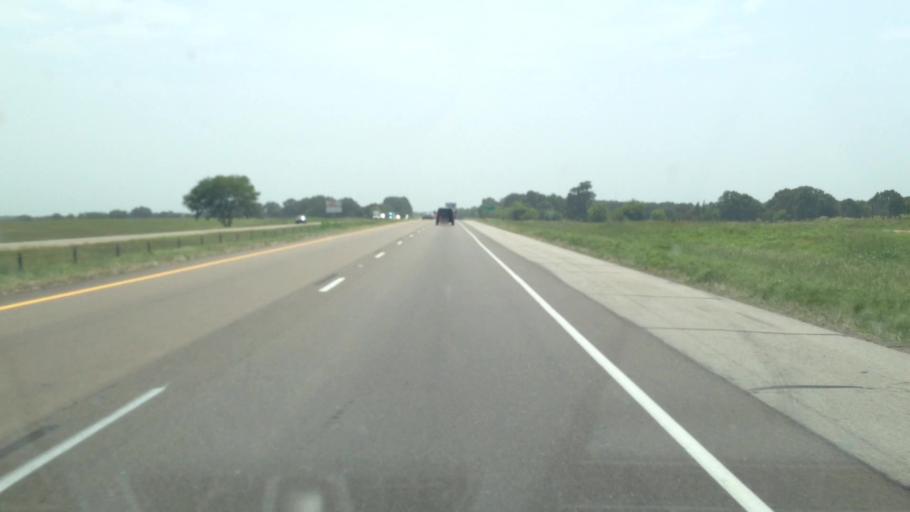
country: US
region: Texas
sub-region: Titus County
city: Mount Pleasant
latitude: 33.2380
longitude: -94.8714
